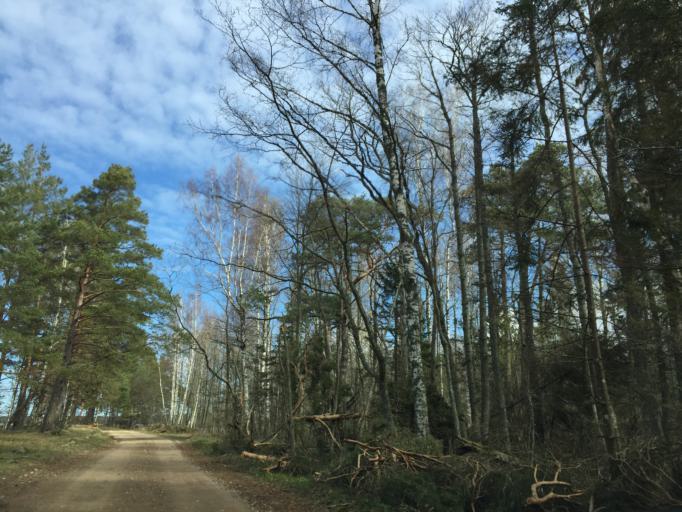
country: LV
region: Salacgrivas
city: Salacgriva
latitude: 57.6020
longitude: 24.3755
